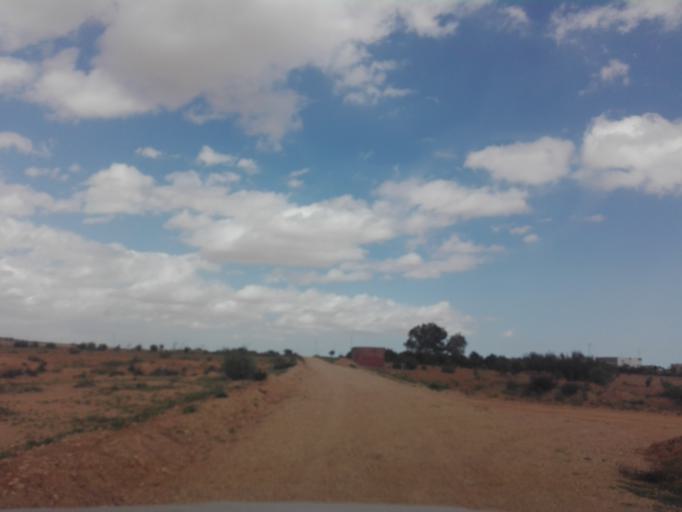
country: TN
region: Safaqis
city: Sfax
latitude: 34.6981
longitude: 10.4310
